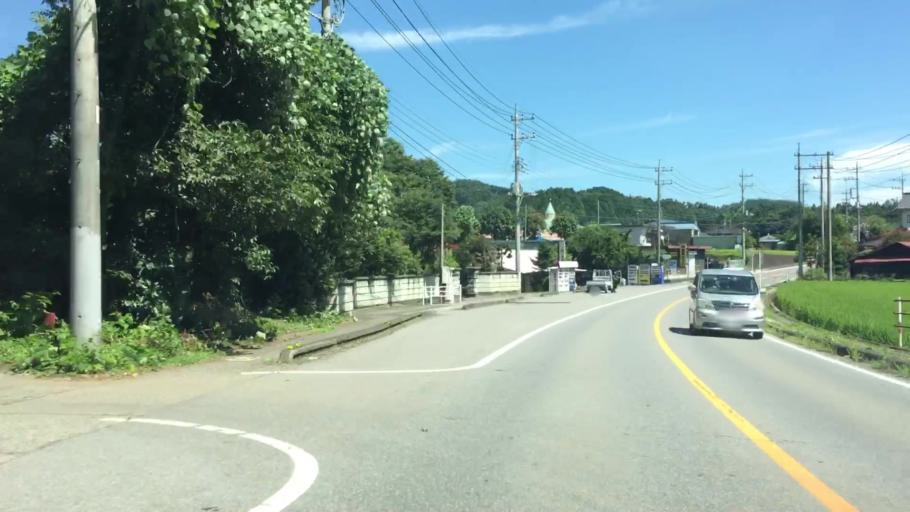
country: JP
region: Tochigi
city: Imaichi
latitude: 36.6920
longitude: 139.7554
